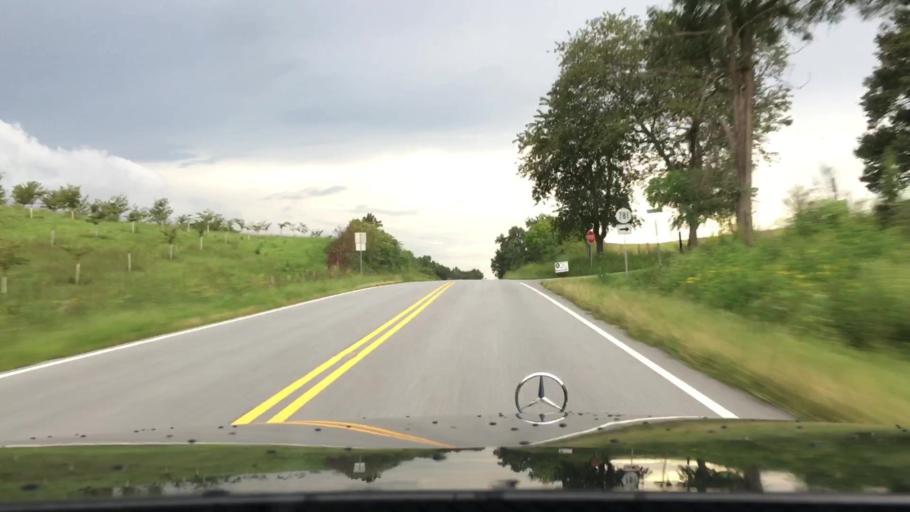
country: US
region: Virginia
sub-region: Nelson County
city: Lovingston
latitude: 37.8056
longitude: -78.9502
